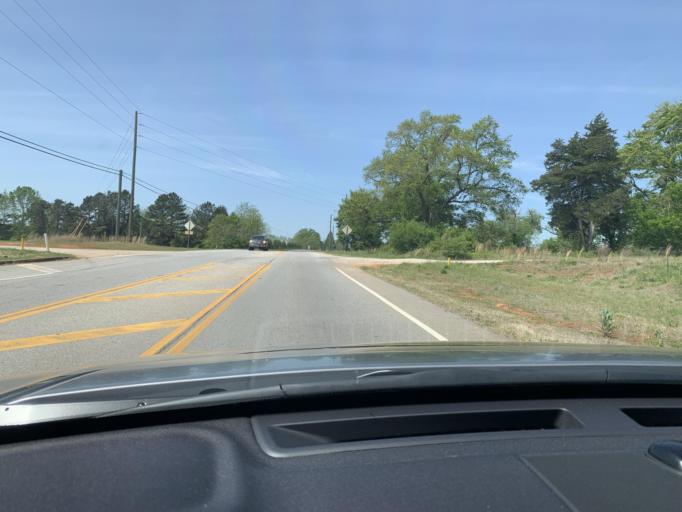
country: US
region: Georgia
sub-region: Oconee County
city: Watkinsville
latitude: 33.8887
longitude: -83.4151
